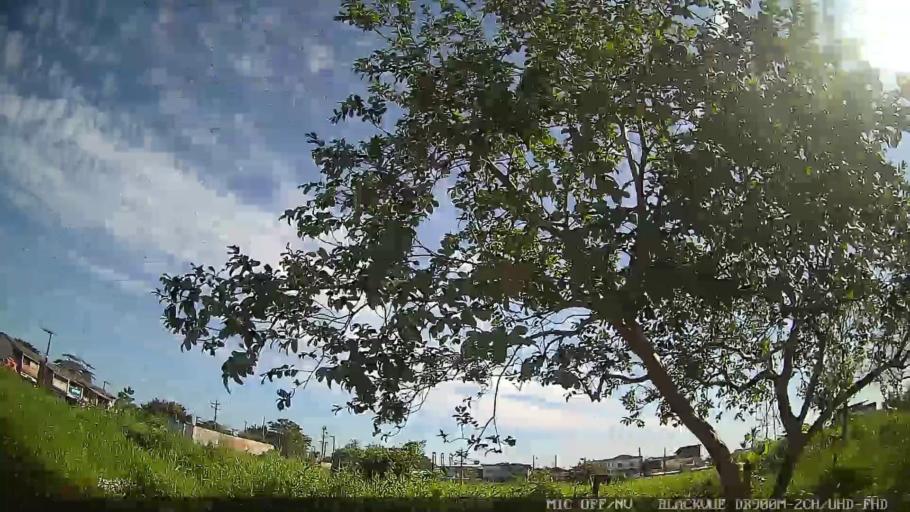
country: BR
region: Sao Paulo
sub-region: Guaruja
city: Guaruja
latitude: -23.9572
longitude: -46.2785
